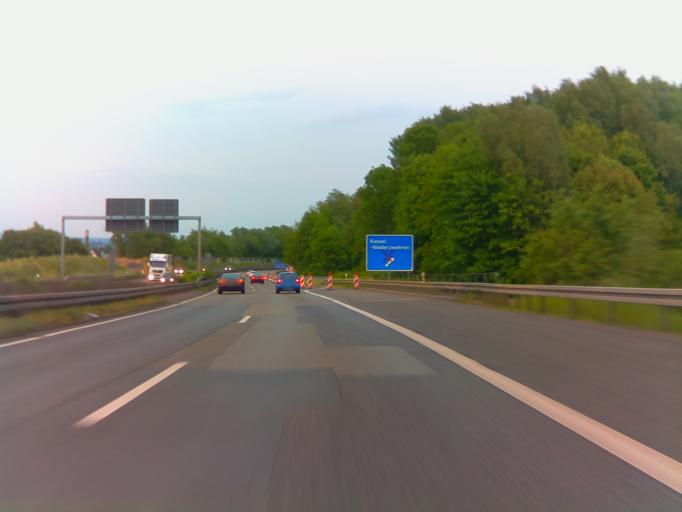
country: DE
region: Hesse
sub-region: Regierungsbezirk Kassel
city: Fuldabruck
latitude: 51.2702
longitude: 9.4581
